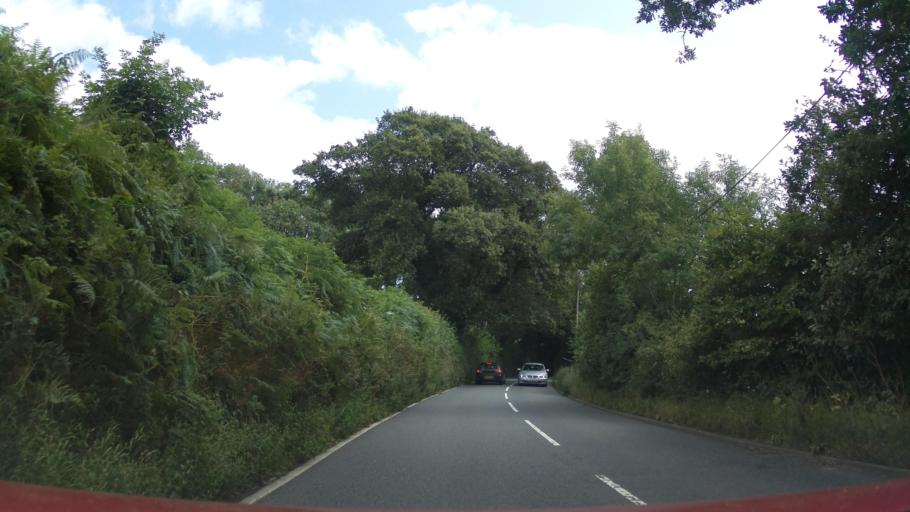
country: GB
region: England
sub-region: Devon
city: Teignmouth
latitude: 50.5662
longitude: -3.5094
